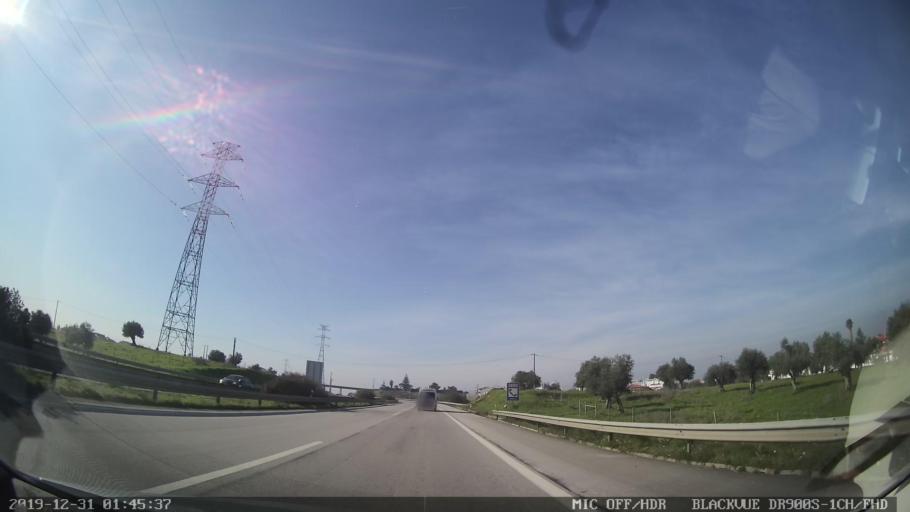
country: PT
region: Santarem
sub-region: Torres Novas
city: Riachos
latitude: 39.4704
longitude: -8.4978
